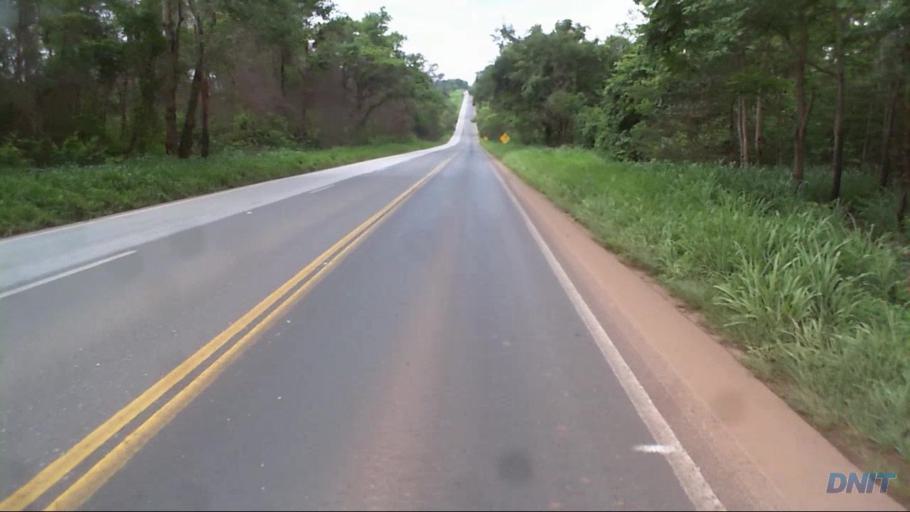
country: BR
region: Goias
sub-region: Uruacu
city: Uruacu
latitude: -14.5881
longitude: -49.1616
